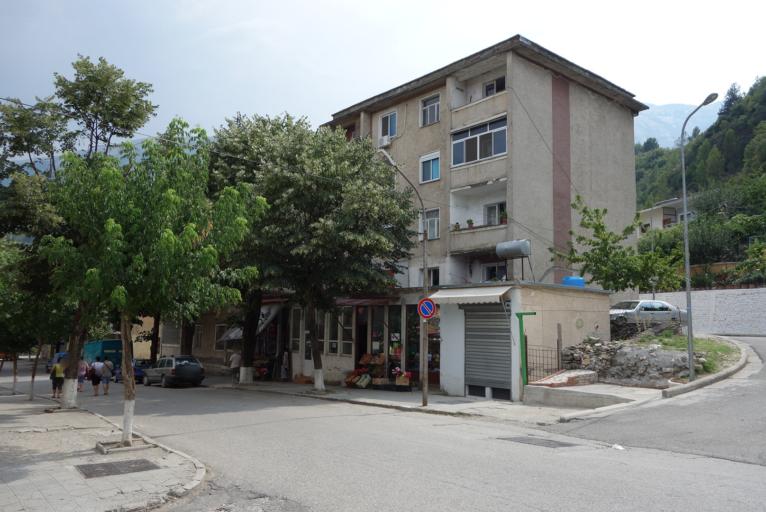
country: AL
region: Gjirokaster
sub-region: Rrethi i Permetit
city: Permet
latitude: 40.2356
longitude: 20.3508
